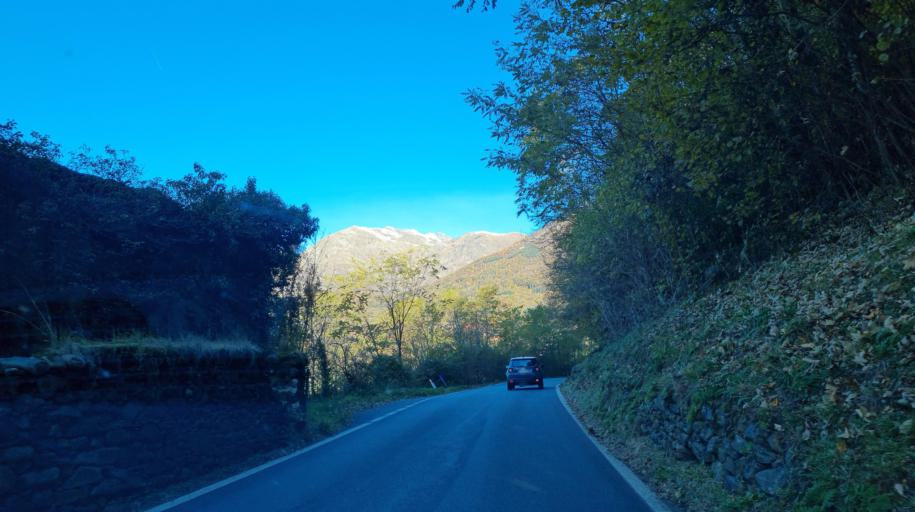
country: IT
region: Piedmont
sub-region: Provincia di Torino
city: Meugliano
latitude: 45.4846
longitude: 7.7817
